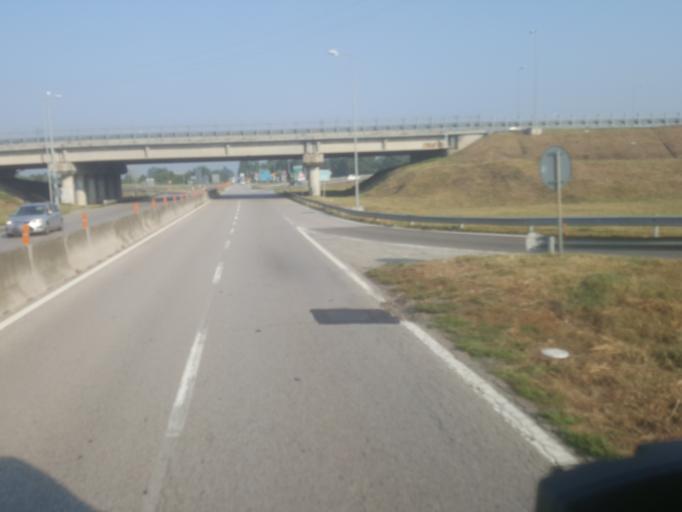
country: IT
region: Emilia-Romagna
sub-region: Provincia di Ravenna
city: Fornace Zarattini
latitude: 44.4272
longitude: 12.1560
